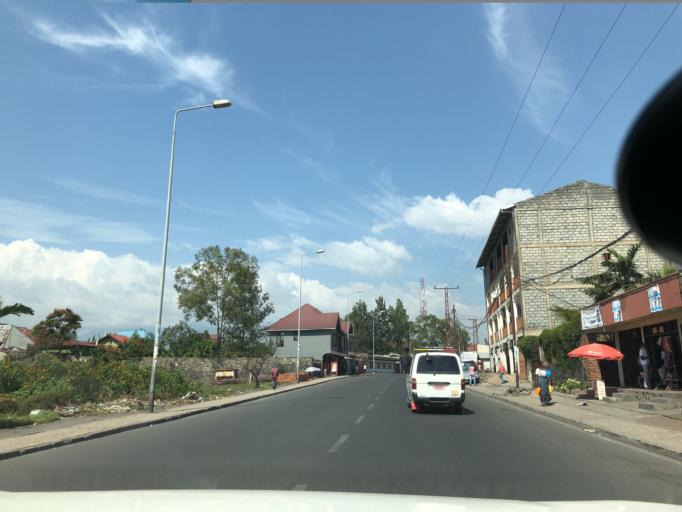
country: CD
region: Nord Kivu
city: Goma
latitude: -1.6596
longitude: 29.1881
